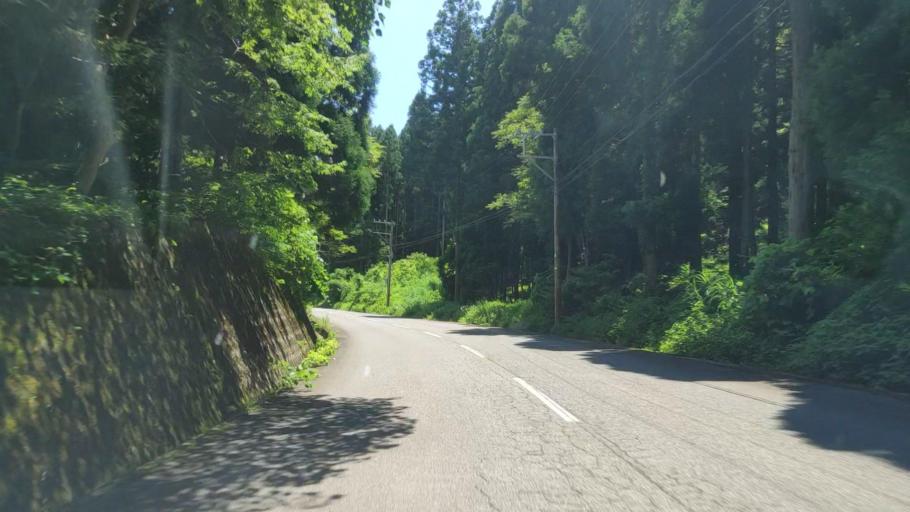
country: JP
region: Fukui
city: Ono
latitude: 35.8811
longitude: 136.5052
